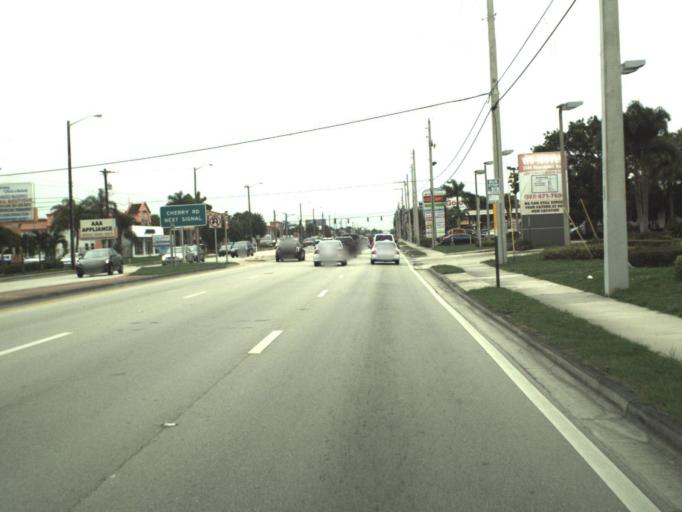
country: US
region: Florida
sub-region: Palm Beach County
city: Haverhill
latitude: 26.6948
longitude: -80.1114
